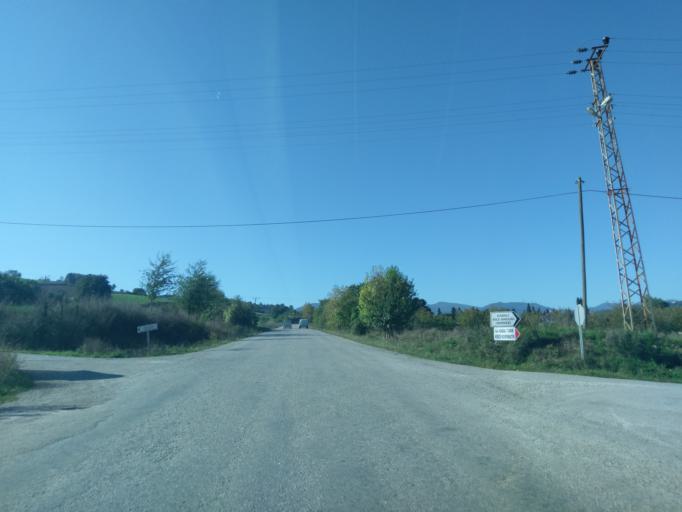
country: TR
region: Sinop
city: Kabali
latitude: 41.8498
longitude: 35.0629
